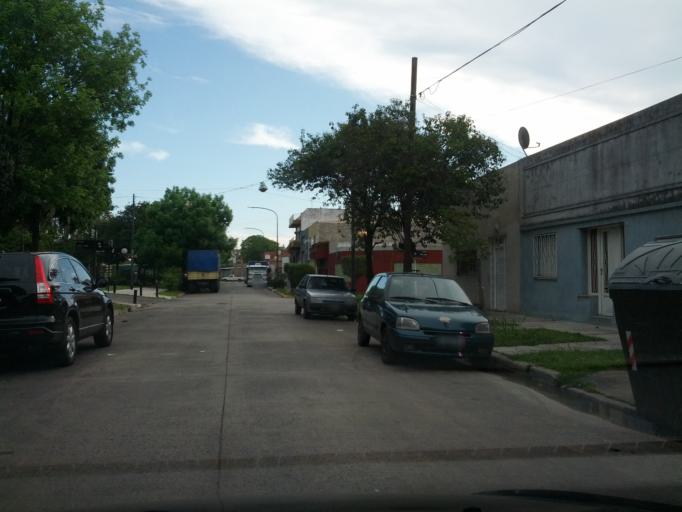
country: AR
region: Buenos Aires F.D.
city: Villa Lugano
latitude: -34.6522
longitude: -58.4287
